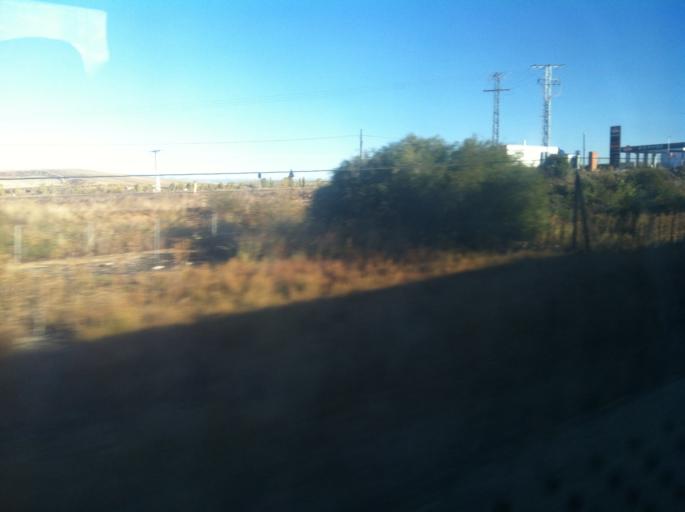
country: ES
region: Castille and Leon
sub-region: Provincia de Palencia
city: Soto de Cerrato
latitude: 41.9855
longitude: -4.4181
